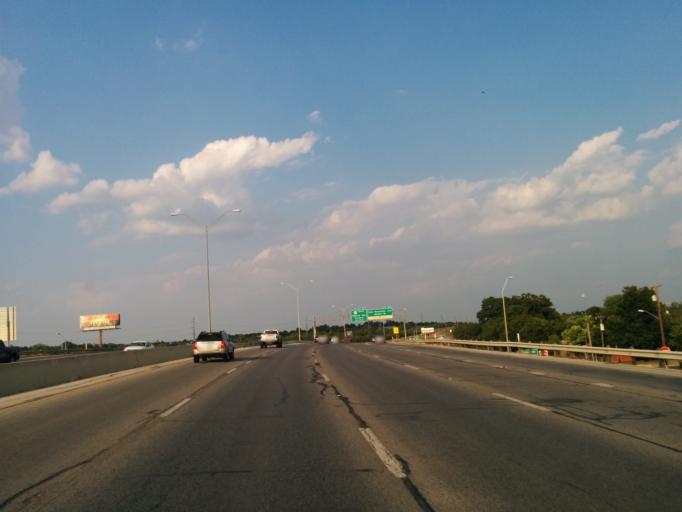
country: US
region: Texas
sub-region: Bexar County
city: San Antonio
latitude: 29.4008
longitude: -98.4706
